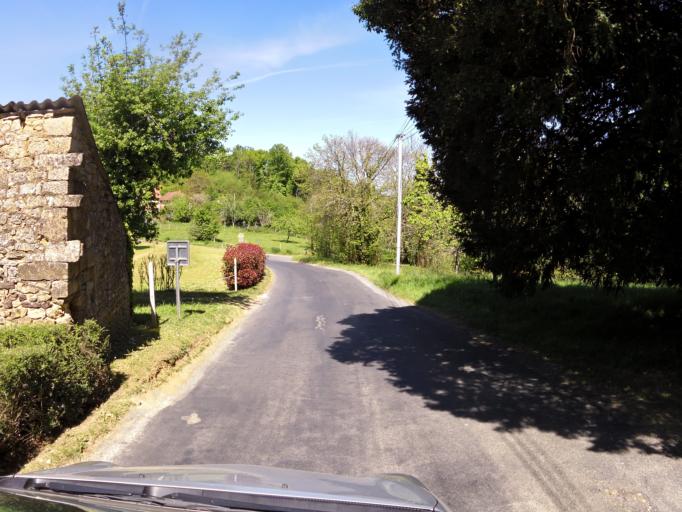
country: FR
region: Aquitaine
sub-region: Departement de la Dordogne
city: Sarlat-la-Caneda
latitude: 44.9195
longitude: 1.1973
